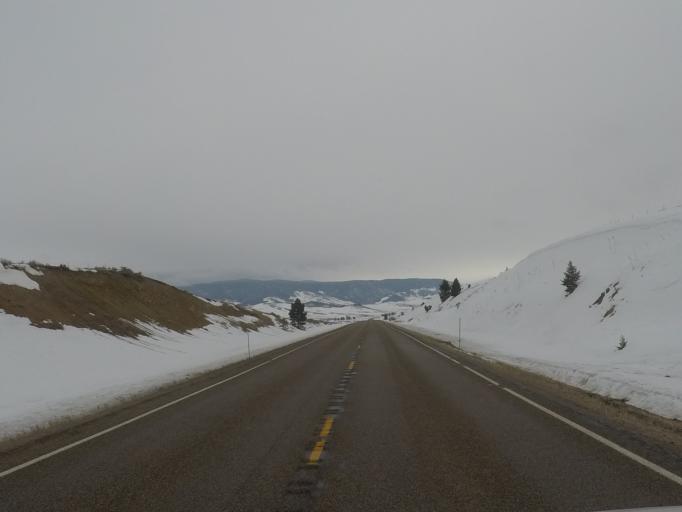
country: US
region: Montana
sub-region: Meagher County
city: White Sulphur Springs
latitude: 46.6216
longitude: -110.8465
